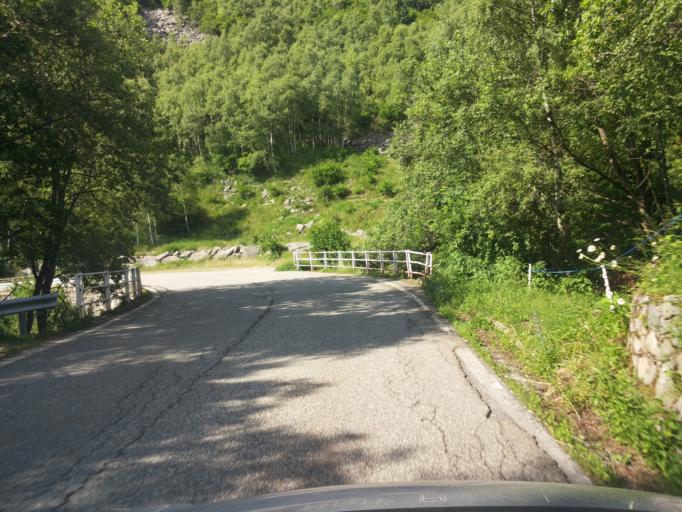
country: IT
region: Piedmont
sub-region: Provincia di Biella
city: Quittengo
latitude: 45.6620
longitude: 8.0308
